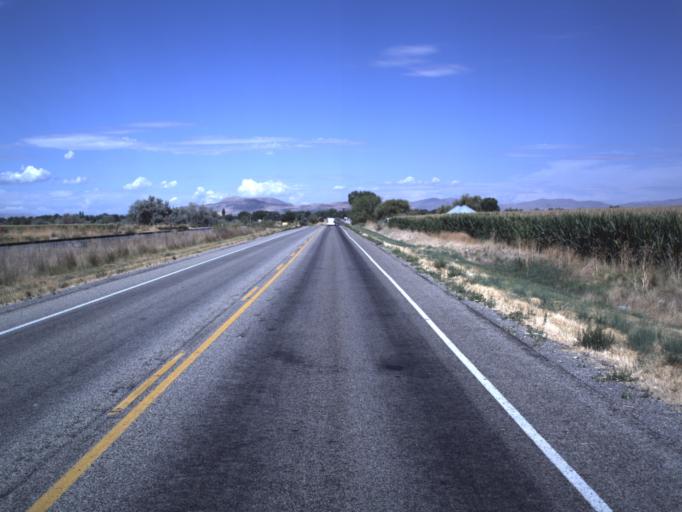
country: US
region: Utah
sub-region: Box Elder County
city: Brigham City
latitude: 41.5413
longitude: -112.0861
